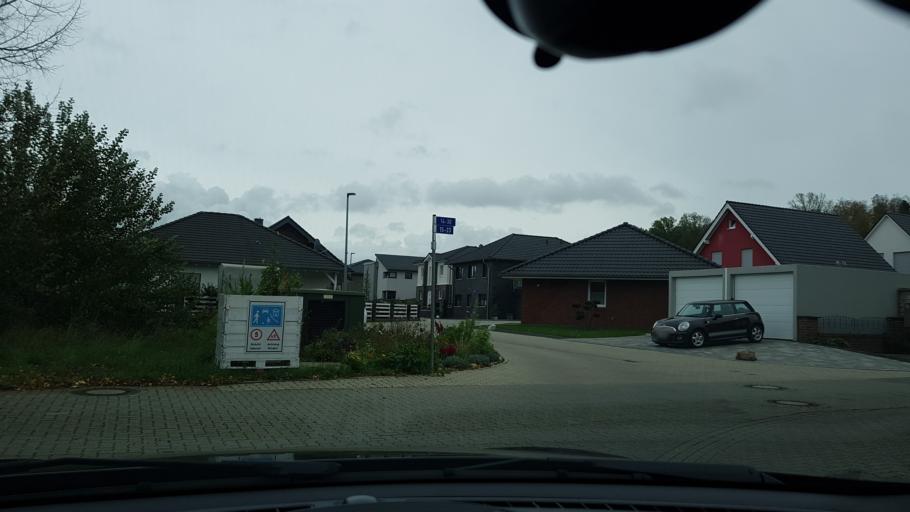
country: DE
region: North Rhine-Westphalia
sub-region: Regierungsbezirk Dusseldorf
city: Grevenbroich
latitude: 51.0420
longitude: 6.5769
